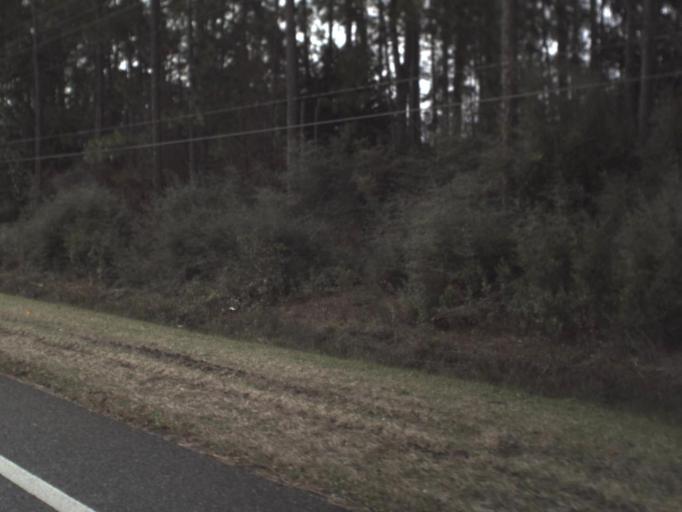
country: US
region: Florida
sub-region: Bay County
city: Youngstown
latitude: 30.2837
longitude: -85.5080
